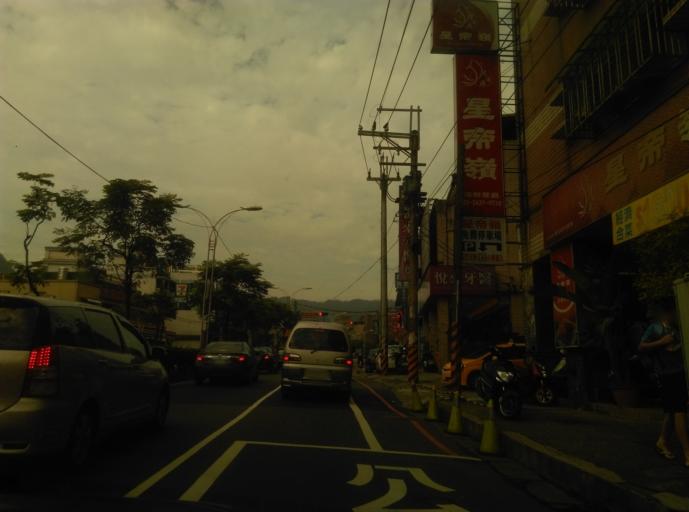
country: TW
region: Taiwan
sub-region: Keelung
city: Keelung
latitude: 25.1542
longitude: 121.6971
